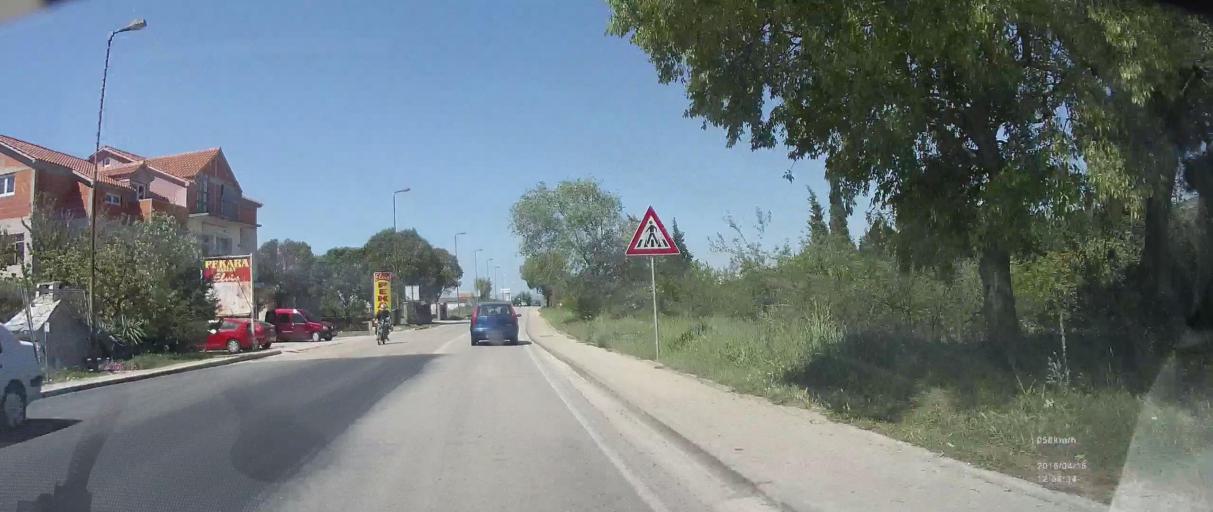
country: HR
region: Sibensko-Kniniska
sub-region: Grad Sibenik
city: Sibenik
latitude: 43.7095
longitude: 15.9219
